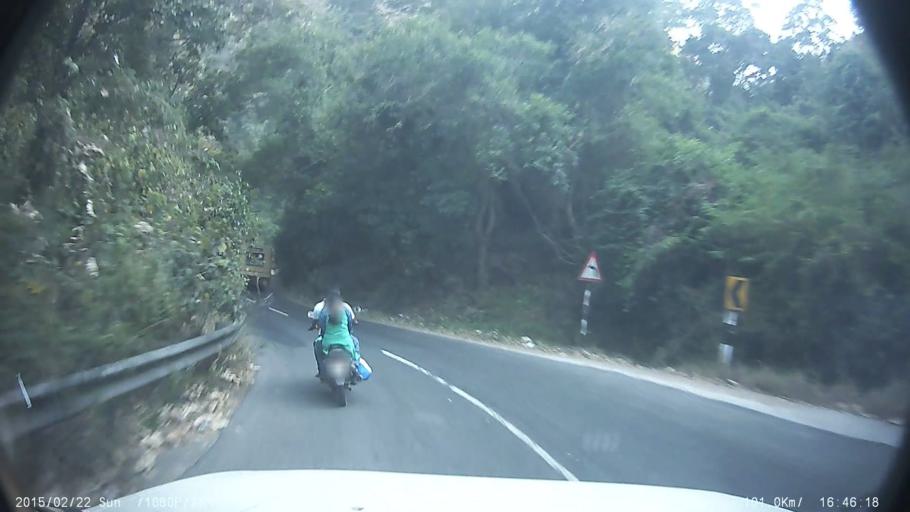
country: IN
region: Tamil Nadu
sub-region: Theni
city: Gudalur
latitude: 9.6202
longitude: 77.1905
